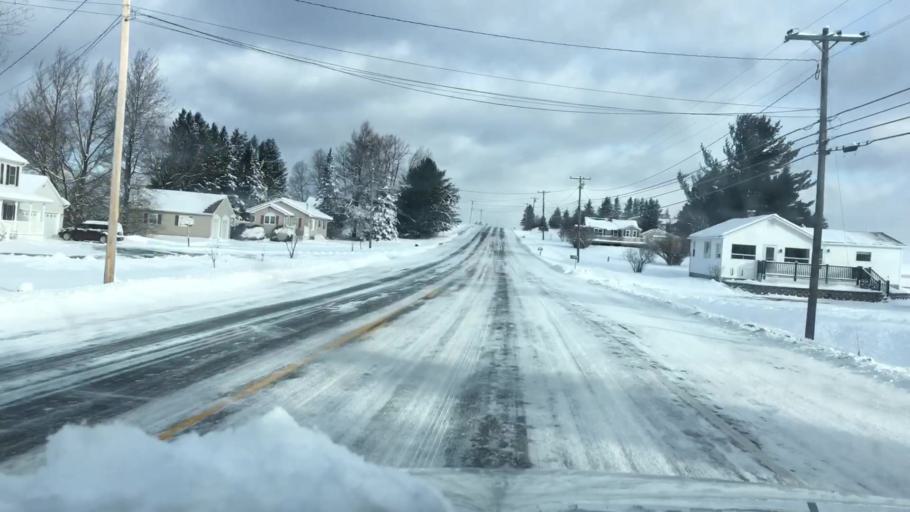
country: US
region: Maine
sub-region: Aroostook County
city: Caribou
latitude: 46.9870
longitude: -68.0306
